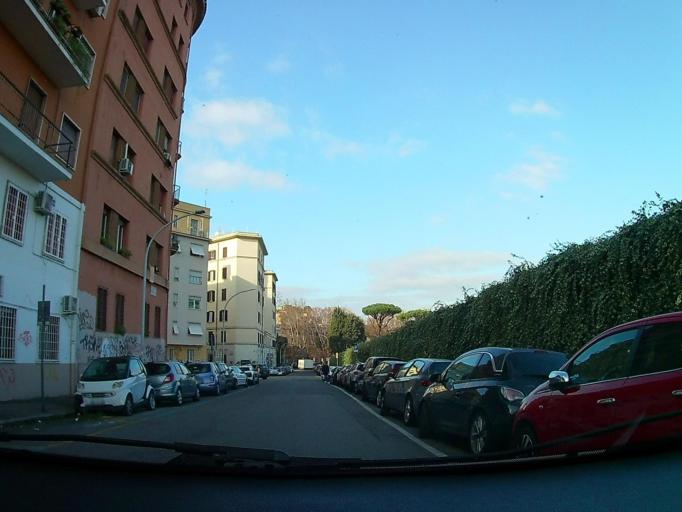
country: IT
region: Latium
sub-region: Citta metropolitana di Roma Capitale
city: Rome
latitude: 41.8737
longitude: 12.4815
